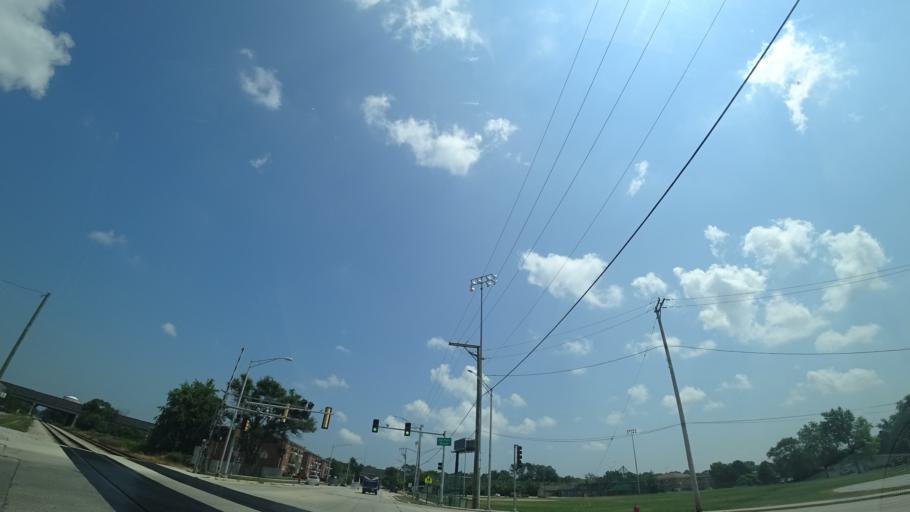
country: US
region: Illinois
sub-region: Cook County
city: Chicago Ridge
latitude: 41.6974
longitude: -87.7882
